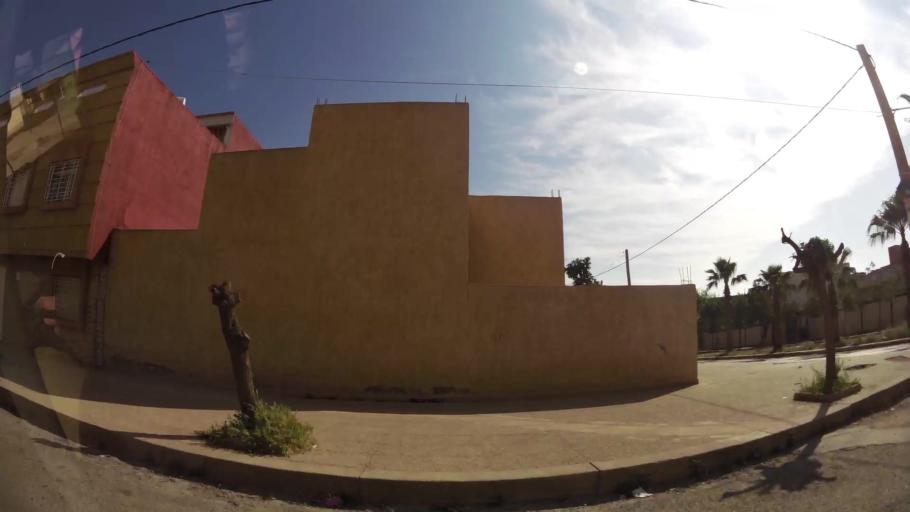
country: MA
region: Oriental
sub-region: Oujda-Angad
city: Oujda
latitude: 34.7107
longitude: -1.8840
